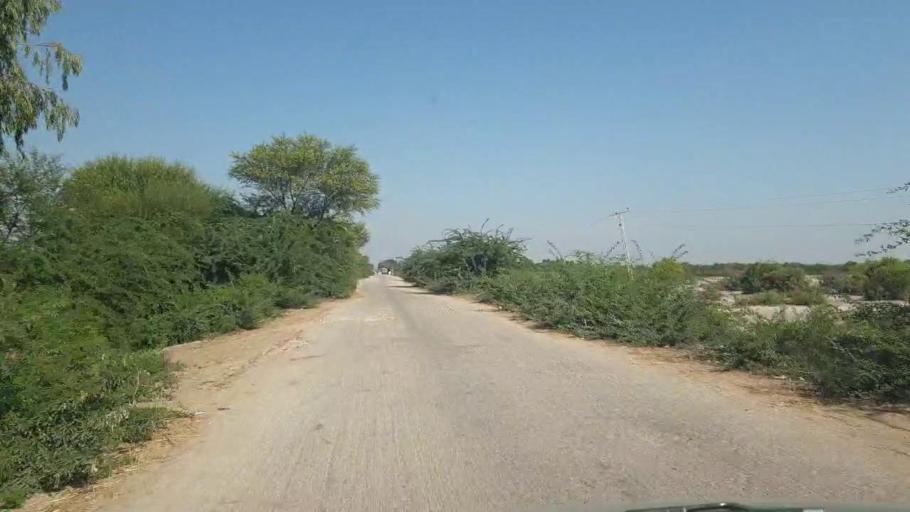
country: PK
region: Sindh
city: Tando Bago
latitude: 24.8149
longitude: 68.9830
